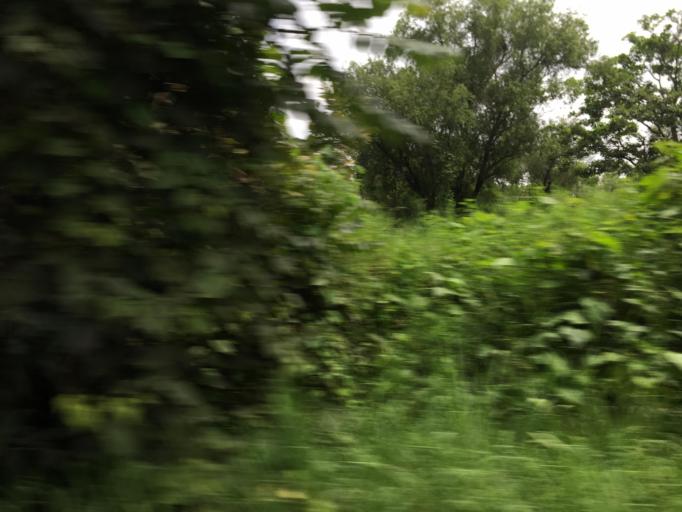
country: GT
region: Guatemala
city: Villa Canales
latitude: 14.4449
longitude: -90.5276
